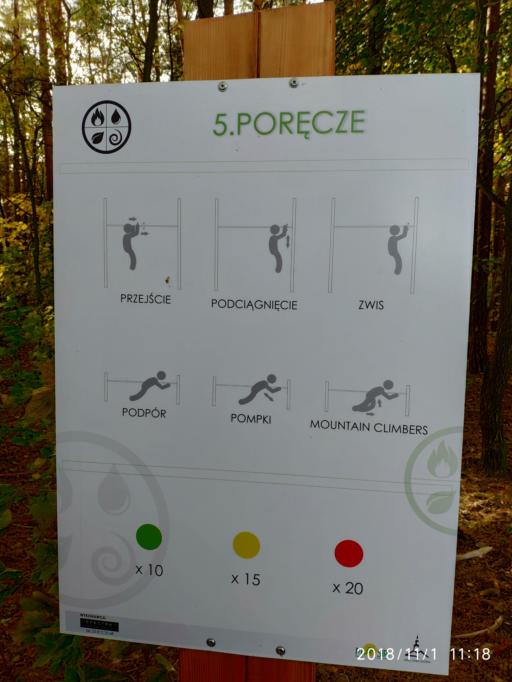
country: PL
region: Lubusz
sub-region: Zielona Gora
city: Zielona Gora
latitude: 51.9342
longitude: 15.5321
